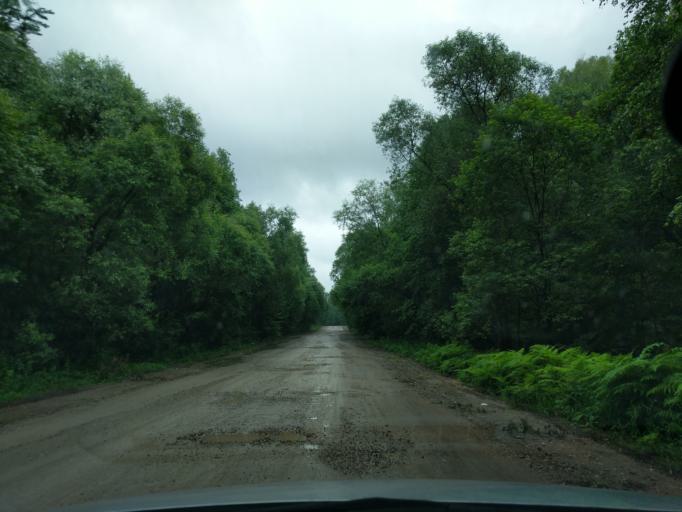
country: RU
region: Kaluga
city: Myatlevo
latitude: 54.8456
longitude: 35.6168
